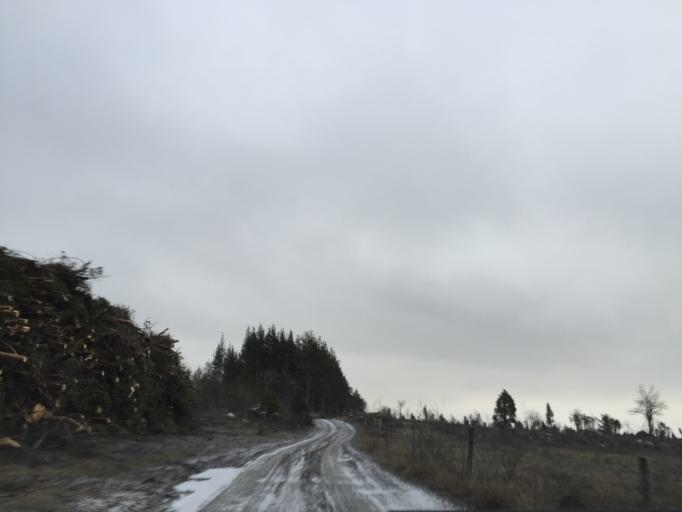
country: EE
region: Saare
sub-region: Orissaare vald
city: Orissaare
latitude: 58.6150
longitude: 23.0799
